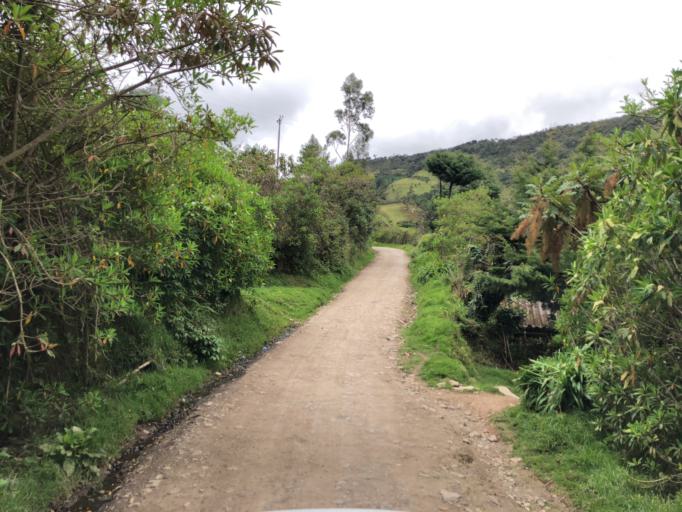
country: CO
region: Cauca
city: Totoro
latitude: 2.5095
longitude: -76.3695
